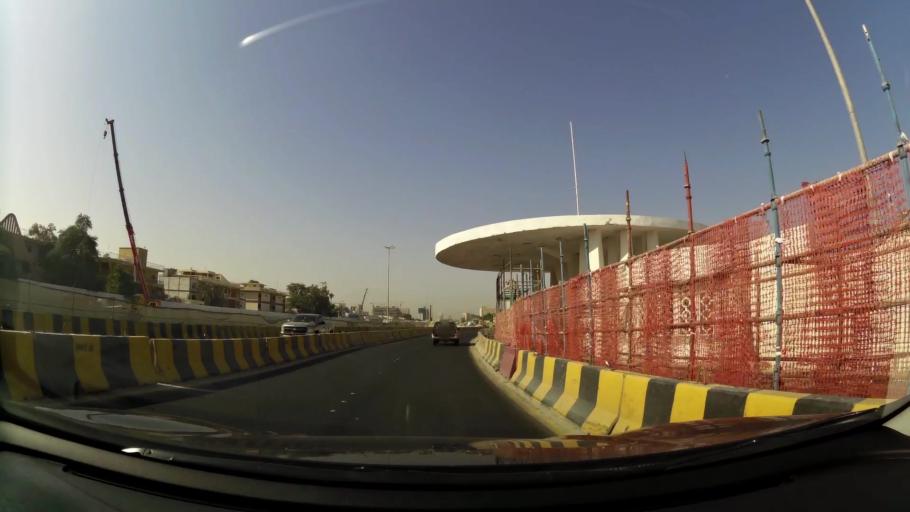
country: KW
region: Al Asimah
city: Ash Shamiyah
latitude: 29.3569
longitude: 47.9534
